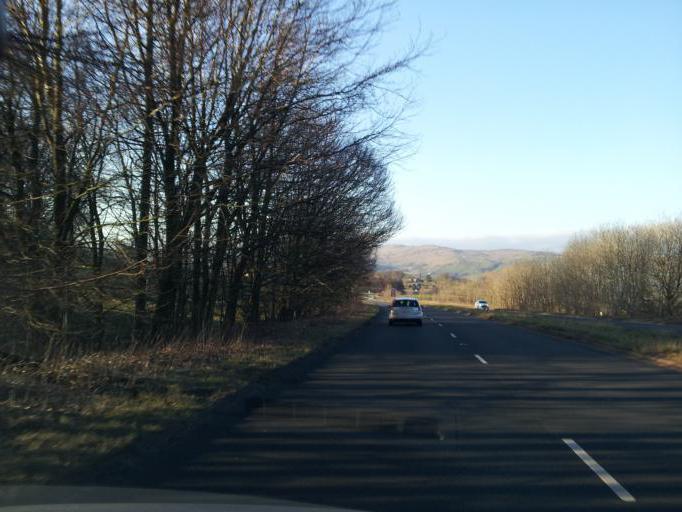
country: GB
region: England
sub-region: Cumbria
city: Kendal
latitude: 54.3383
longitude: -2.7719
